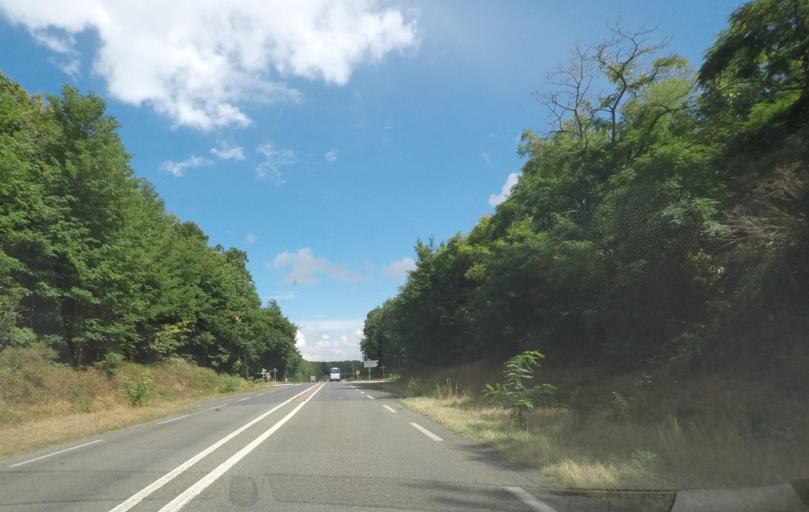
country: FR
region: Pays de la Loire
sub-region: Departement de la Sarthe
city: Beaufay
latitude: 48.1394
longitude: 0.3785
